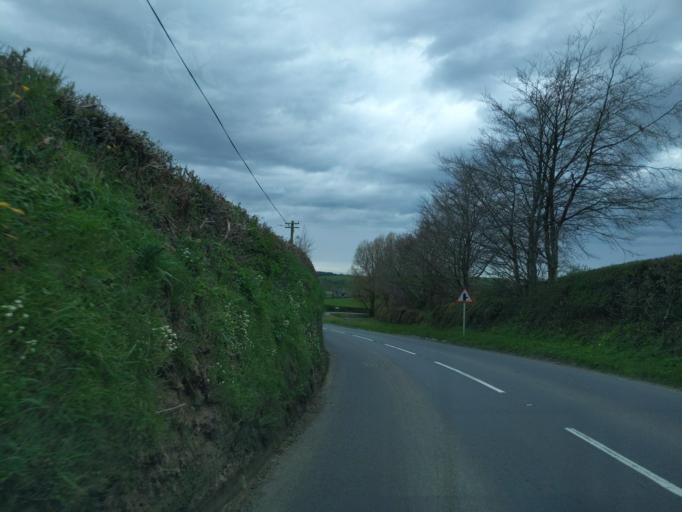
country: GB
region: England
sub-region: Devon
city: Great Torrington
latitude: 50.9332
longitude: -4.0865
